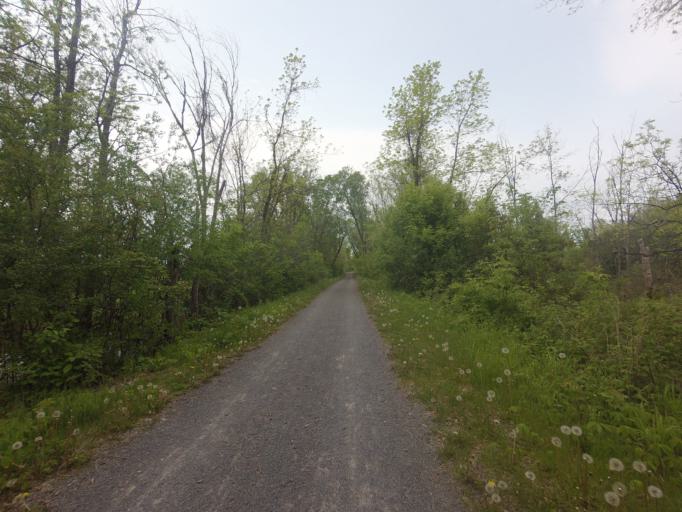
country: CA
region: Ontario
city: Kingston
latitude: 44.2923
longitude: -76.5586
